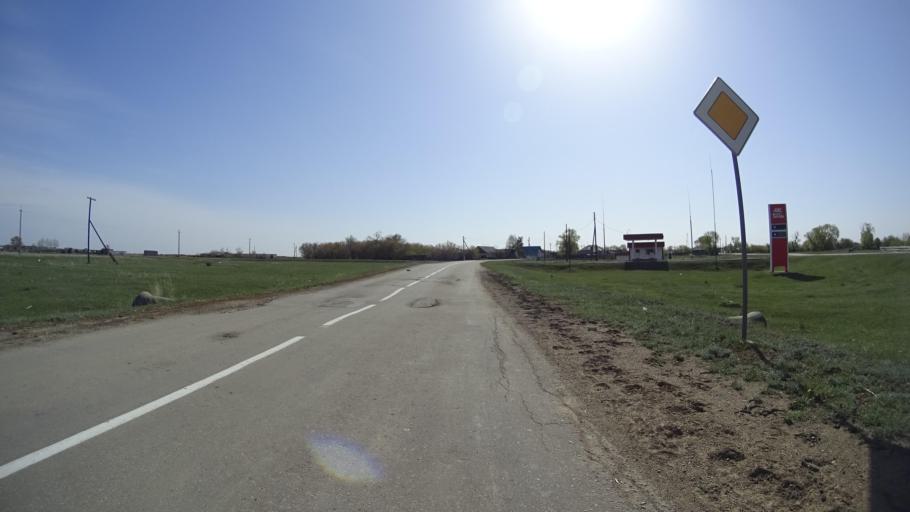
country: RU
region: Chelyabinsk
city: Chesma
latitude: 53.8027
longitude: 61.0148
